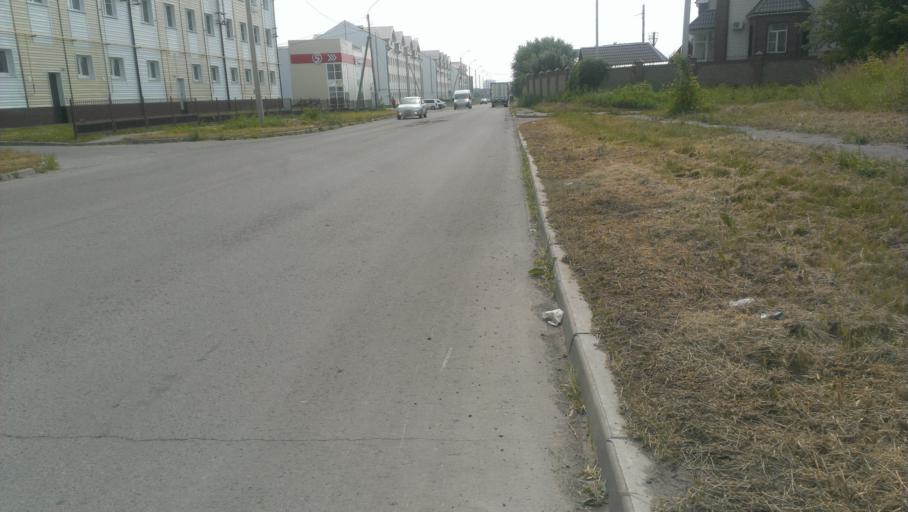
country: RU
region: Altai Krai
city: Novosilikatnyy
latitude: 53.3616
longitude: 83.6562
